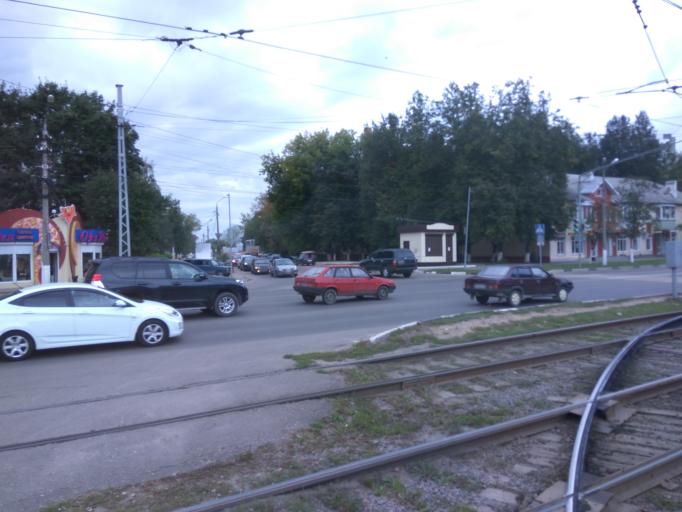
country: RU
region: Moskovskaya
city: Kolomna
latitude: 55.0807
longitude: 38.7627
